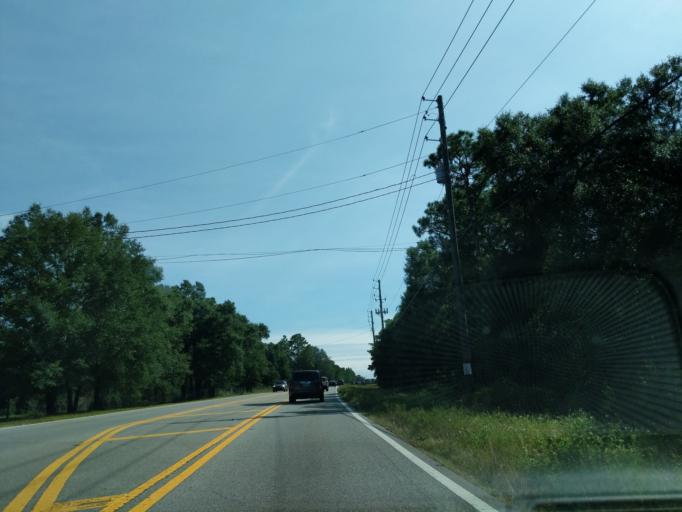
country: US
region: Florida
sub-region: Okaloosa County
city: Crestview
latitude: 30.7258
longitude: -86.6164
